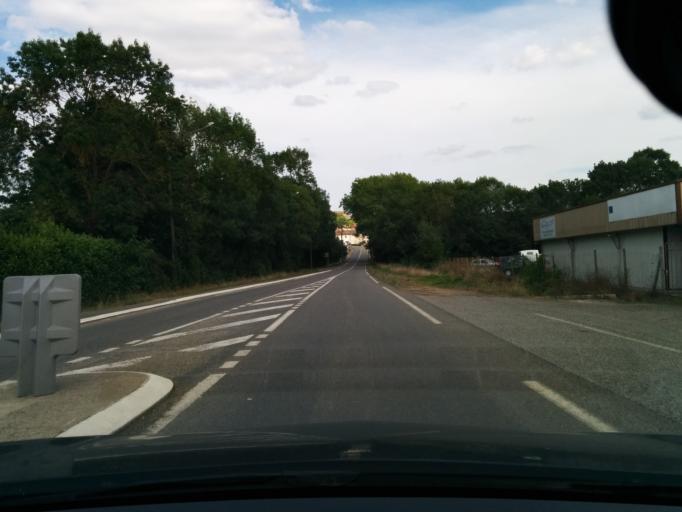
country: FR
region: Midi-Pyrenees
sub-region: Departement du Gers
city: Aubiet
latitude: 43.6465
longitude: 0.7766
